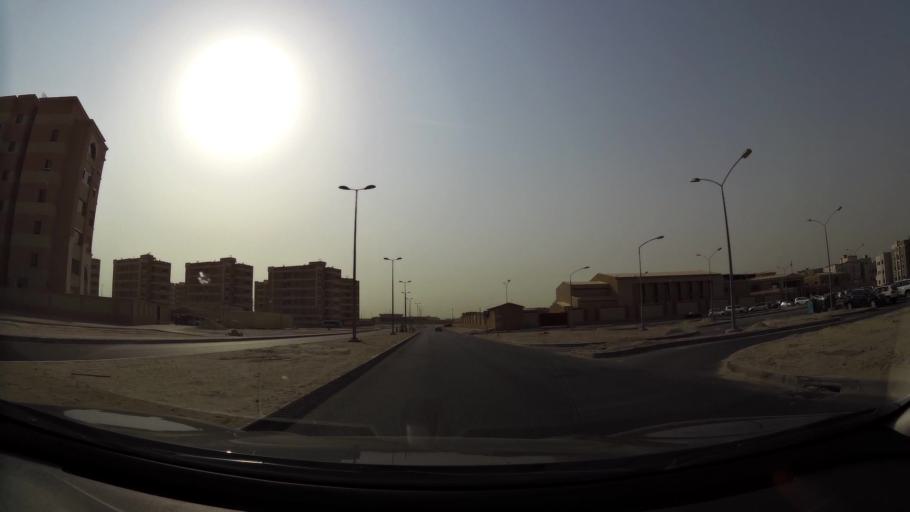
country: KW
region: Al Asimah
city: Ar Rabiyah
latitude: 29.3251
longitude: 47.8157
